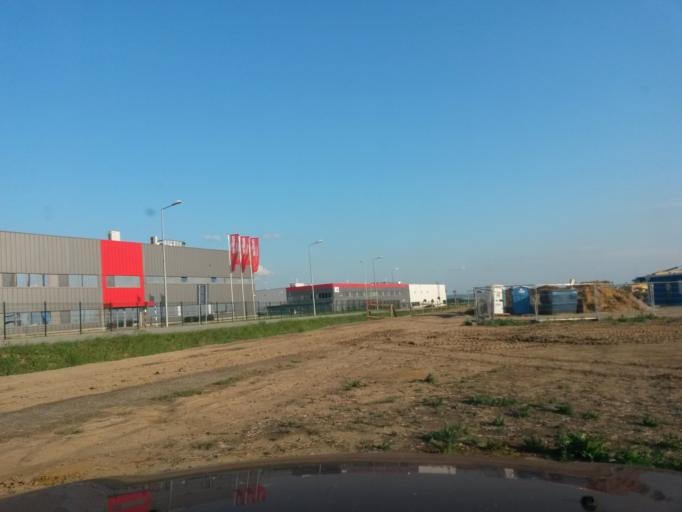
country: SK
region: Kosicky
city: Moldava nad Bodvou
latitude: 48.6170
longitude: 21.1391
